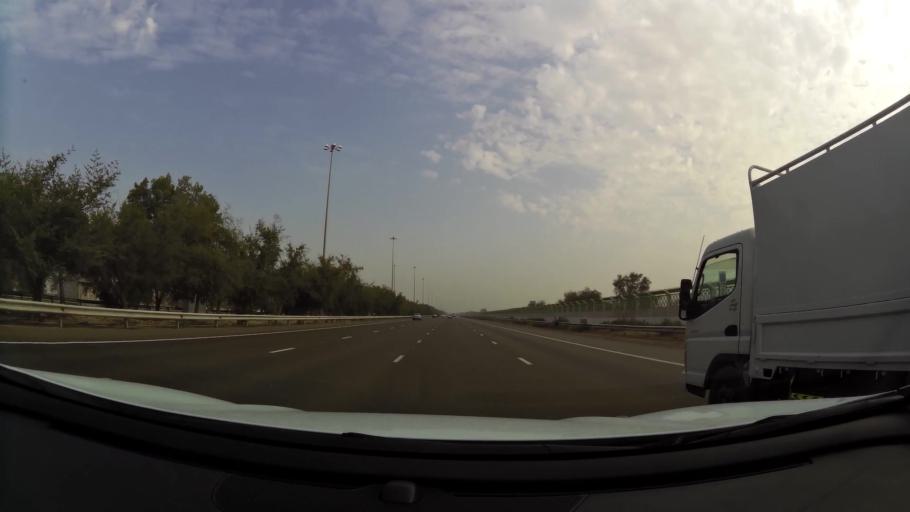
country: AE
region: Abu Dhabi
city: Abu Dhabi
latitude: 24.5890
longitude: 54.7028
